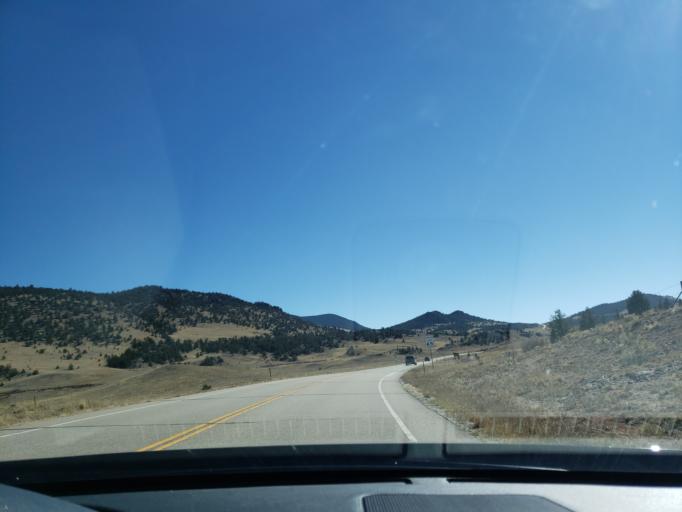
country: US
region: Colorado
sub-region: Chaffee County
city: Salida
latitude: 38.8620
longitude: -105.6585
